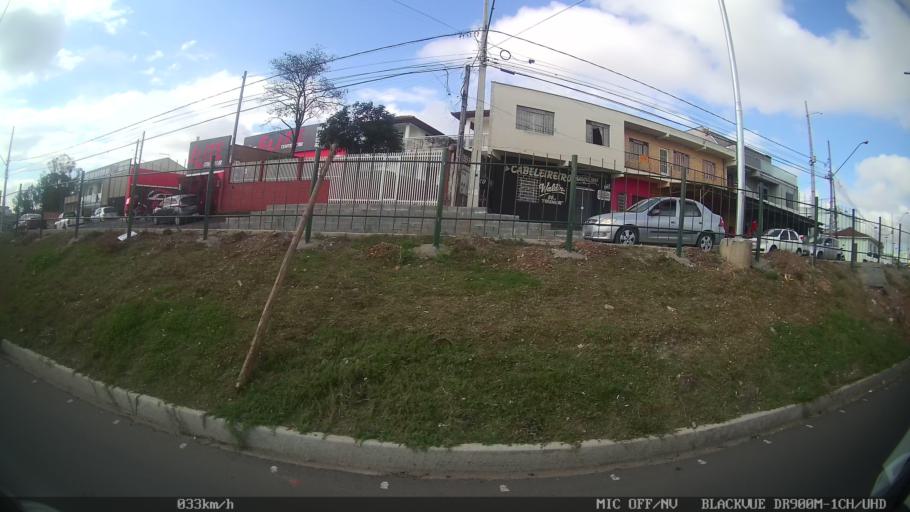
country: BR
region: Parana
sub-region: Pinhais
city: Pinhais
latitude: -25.3747
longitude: -49.1863
